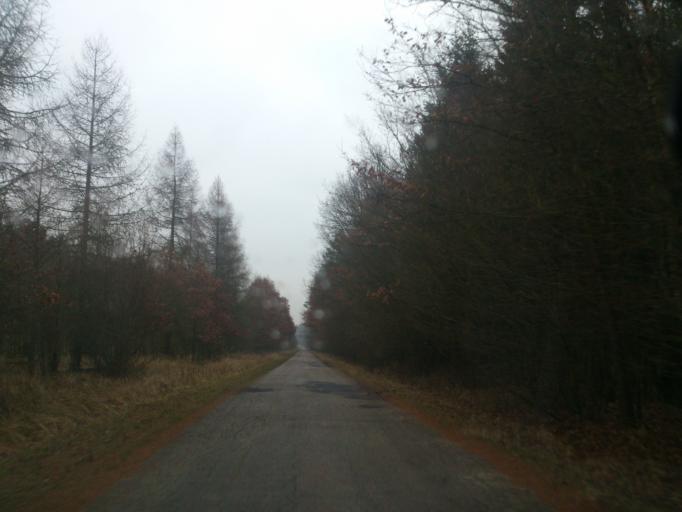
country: PL
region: Kujawsko-Pomorskie
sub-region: Powiat golubsko-dobrzynski
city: Radomin
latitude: 53.1599
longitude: 19.1573
